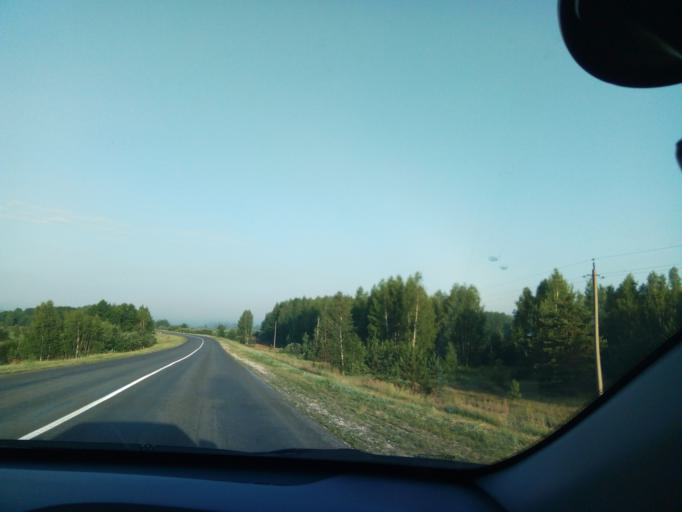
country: RU
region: Nizjnij Novgorod
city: Voznesenskoye
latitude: 54.8677
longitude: 42.9559
